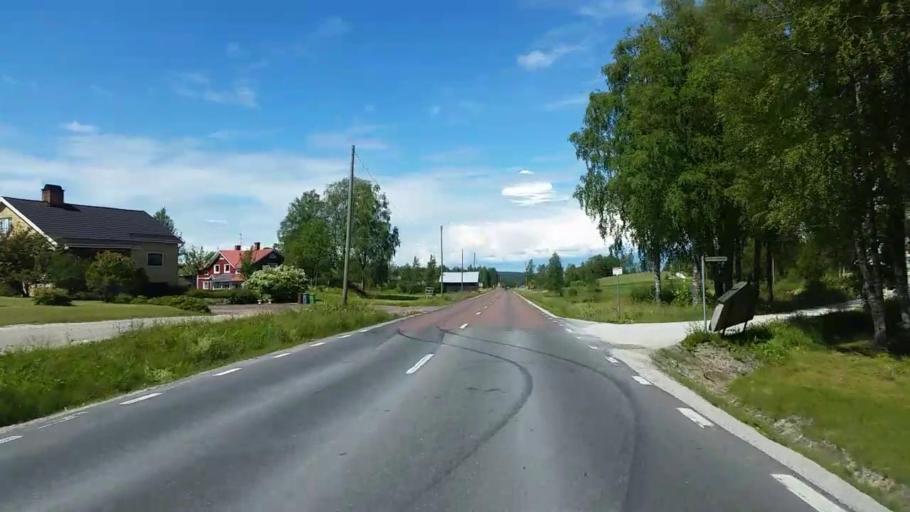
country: SE
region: Dalarna
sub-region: Rattviks Kommun
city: Raettvik
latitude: 61.0372
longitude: 15.2004
